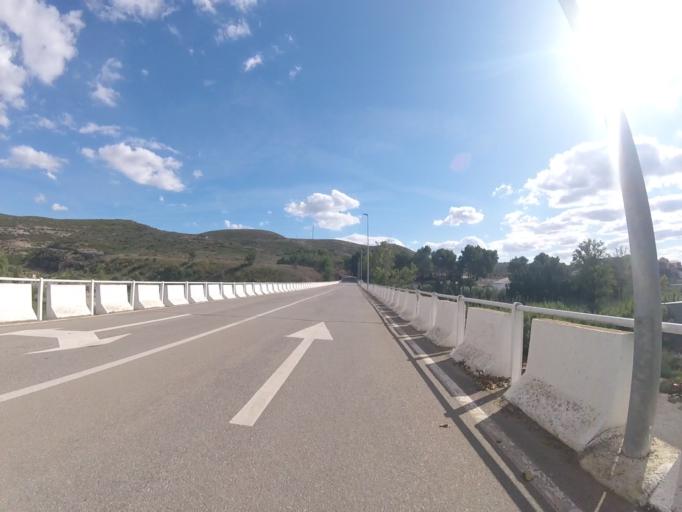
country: ES
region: Valencia
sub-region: Provincia de Castello
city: Cuevas de Vinroma
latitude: 40.3153
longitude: 0.1234
